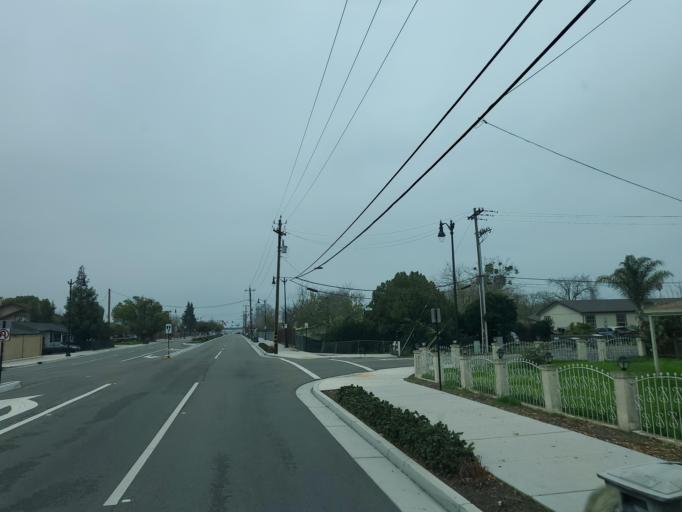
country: US
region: California
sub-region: San Joaquin County
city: Lathrop
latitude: 37.8264
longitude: -121.2823
